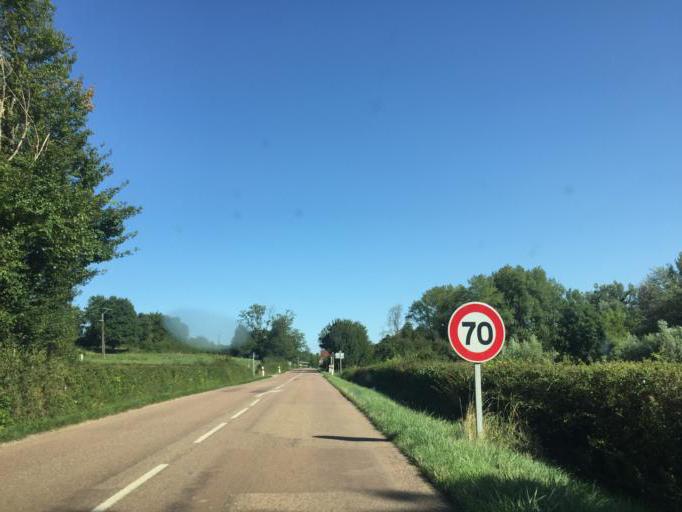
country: FR
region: Bourgogne
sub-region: Departement de la Nievre
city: Clamecy
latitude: 47.4719
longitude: 3.4429
